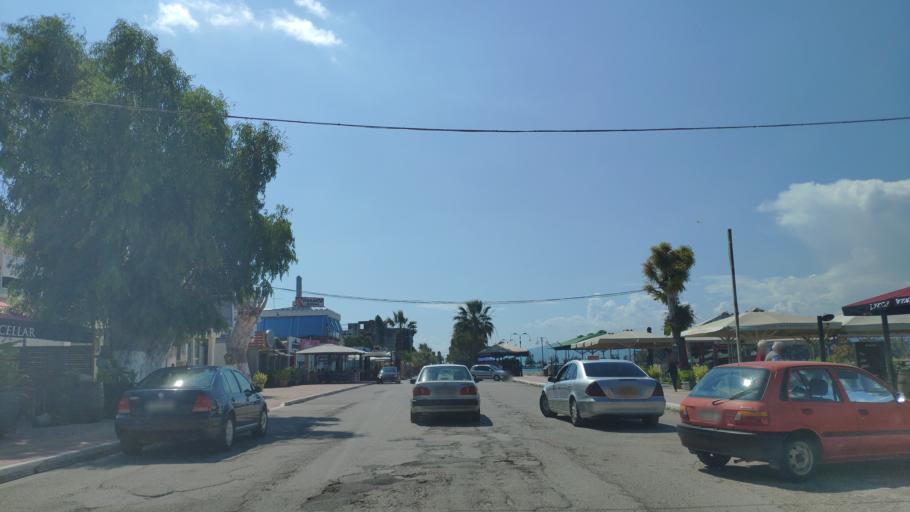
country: GR
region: Central Greece
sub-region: Nomos Evvoias
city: Eretria
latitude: 38.3913
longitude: 23.7967
